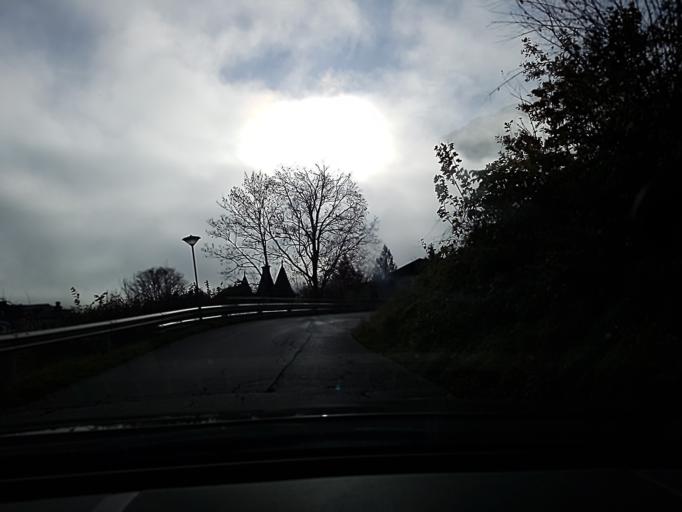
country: AT
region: Salzburg
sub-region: Politischer Bezirk Sankt Johann im Pongau
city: Schwarzach im Pongau
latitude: 47.3225
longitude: 13.1506
